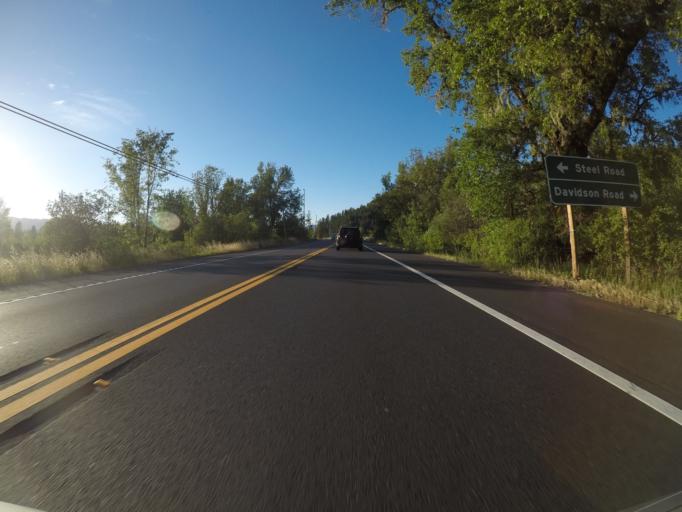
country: US
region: California
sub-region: Mendocino County
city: Laytonville
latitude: 39.6504
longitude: -123.4764
